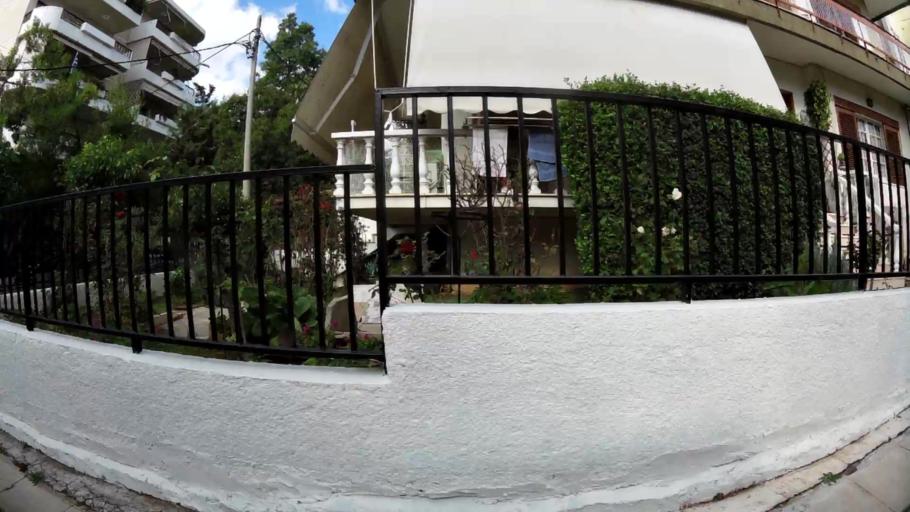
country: GR
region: Attica
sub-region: Nomarchia Athinas
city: Marousi
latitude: 38.0547
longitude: 23.8164
